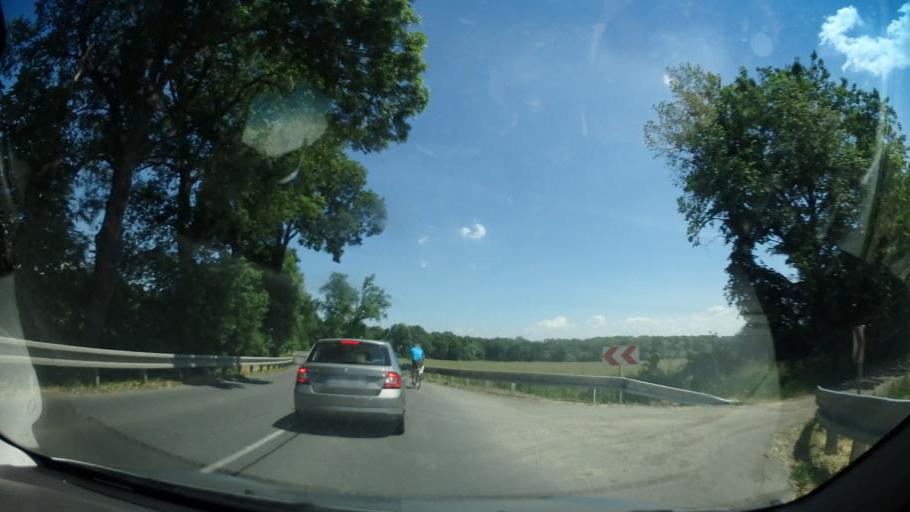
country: CZ
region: Zlin
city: Chropyne
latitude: 49.3495
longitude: 17.3349
